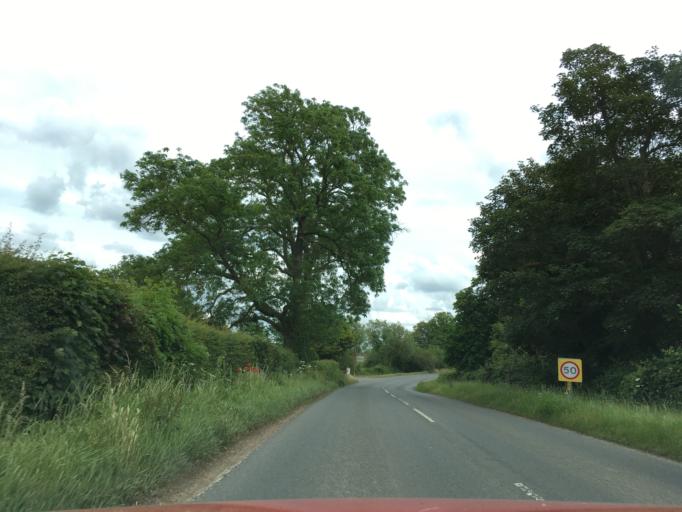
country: GB
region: England
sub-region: Wiltshire
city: Lyneham
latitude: 51.5639
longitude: -2.0007
